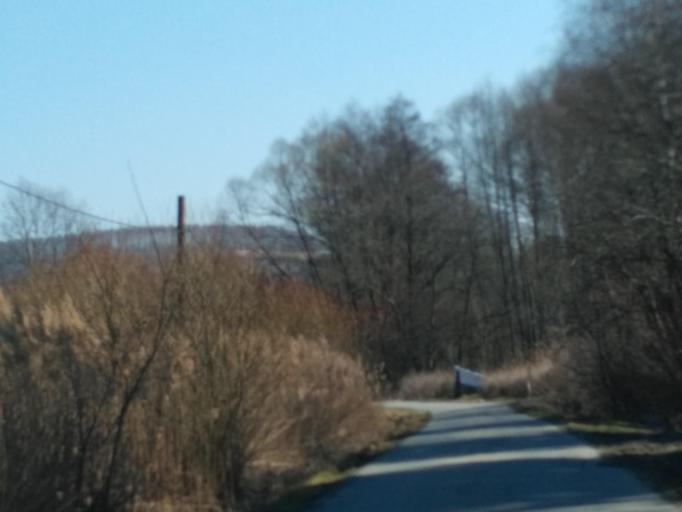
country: PL
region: Subcarpathian Voivodeship
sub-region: Powiat ropczycko-sedziszowski
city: Iwierzyce
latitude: 49.9541
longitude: 21.7386
